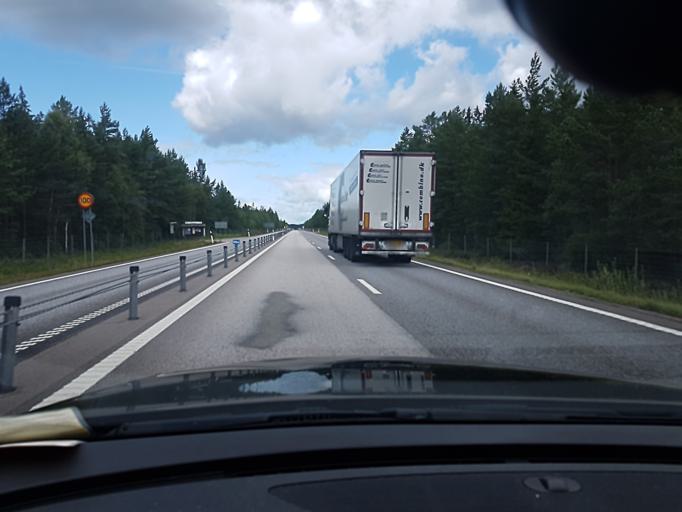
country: SE
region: Kronoberg
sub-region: Lessebo Kommun
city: Hovmantorp
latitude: 56.7980
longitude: 15.1170
